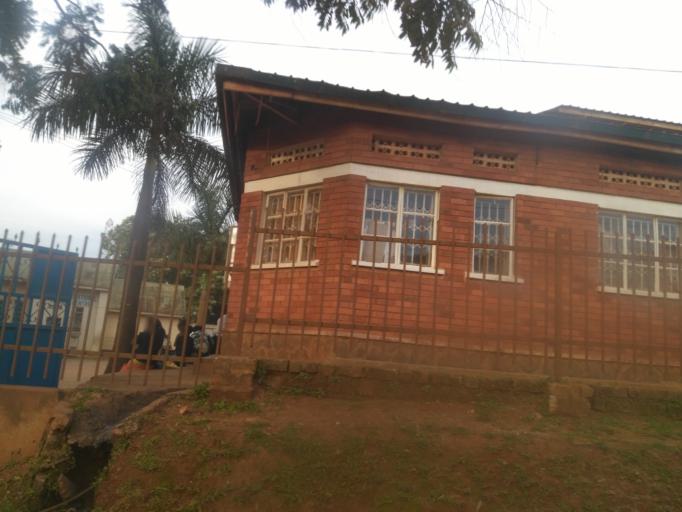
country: UG
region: Central Region
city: Kampala Central Division
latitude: 0.3458
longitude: 32.5747
